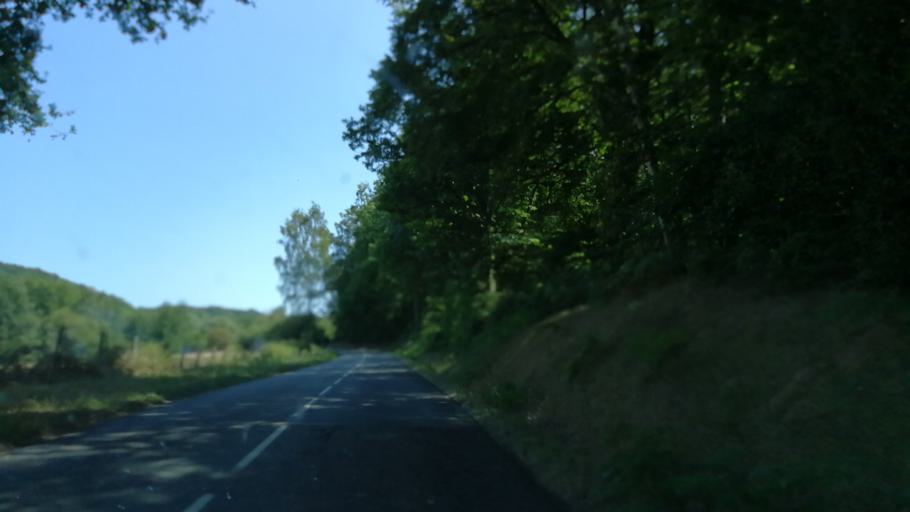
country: FR
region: Ile-de-France
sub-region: Departement des Yvelines
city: Cernay-la-Ville
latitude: 48.6774
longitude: 1.9496
